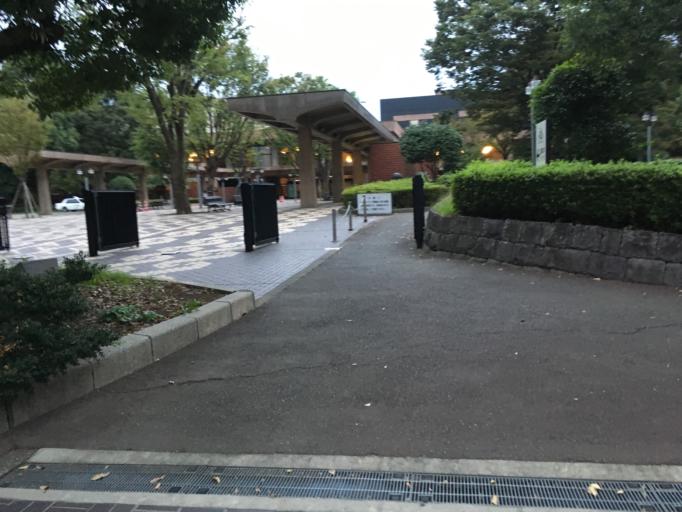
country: JP
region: Kumamoto
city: Kumamoto
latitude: 32.8018
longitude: 130.7271
